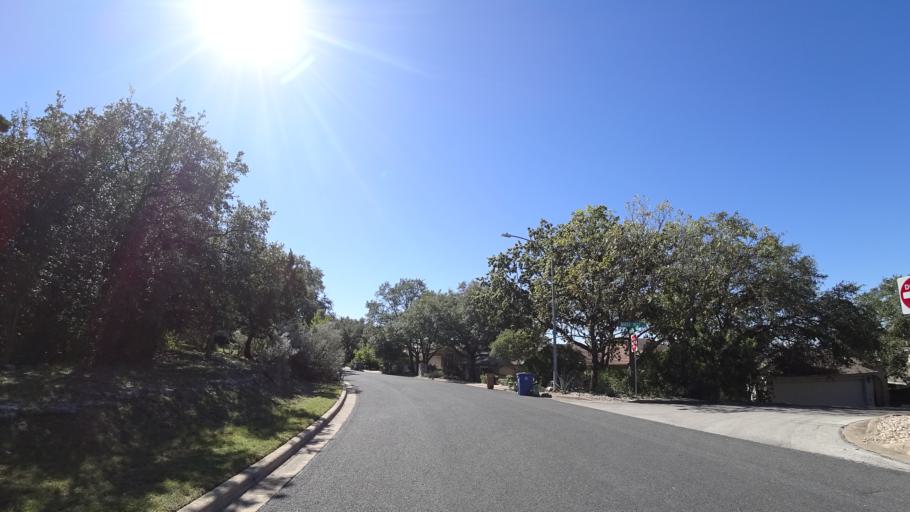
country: US
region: Texas
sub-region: Travis County
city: West Lake Hills
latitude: 30.3468
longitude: -97.7822
